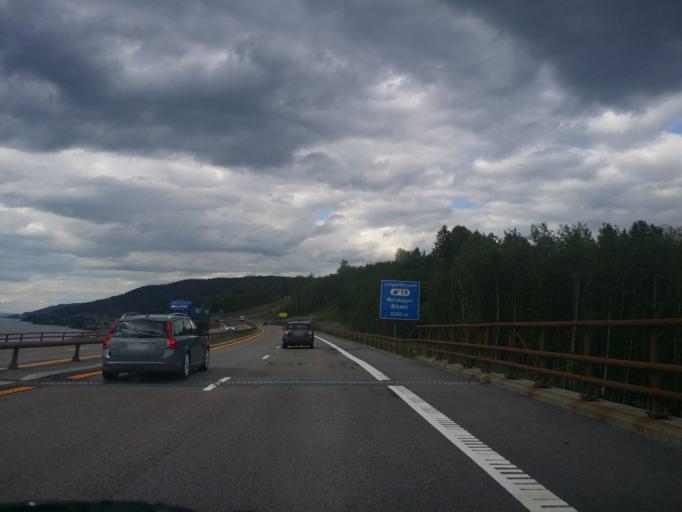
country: NO
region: Akershus
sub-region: Eidsvoll
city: Eidsvoll
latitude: 60.4014
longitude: 11.2354
